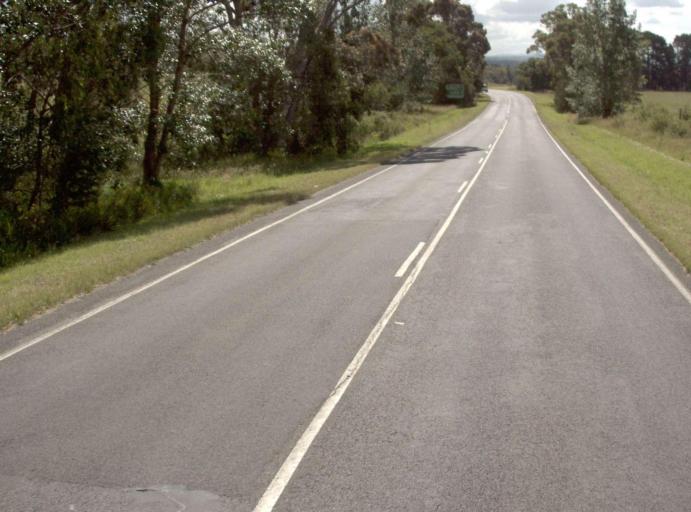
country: AU
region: Victoria
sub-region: Latrobe
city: Moe
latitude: -38.1742
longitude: 146.3215
